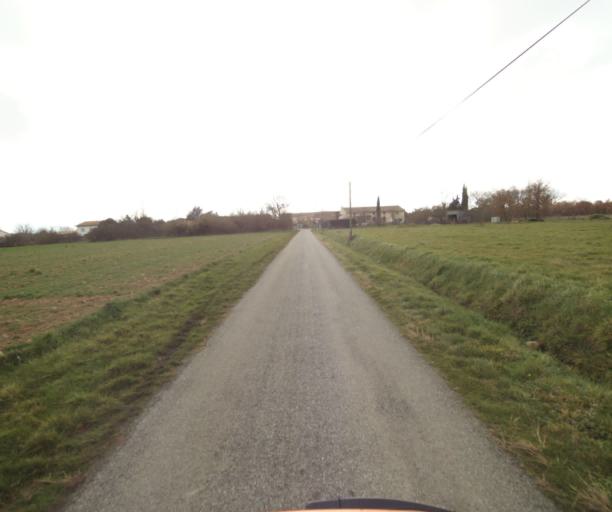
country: FR
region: Languedoc-Roussillon
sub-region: Departement de l'Aude
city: Belpech
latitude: 43.1724
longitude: 1.6893
